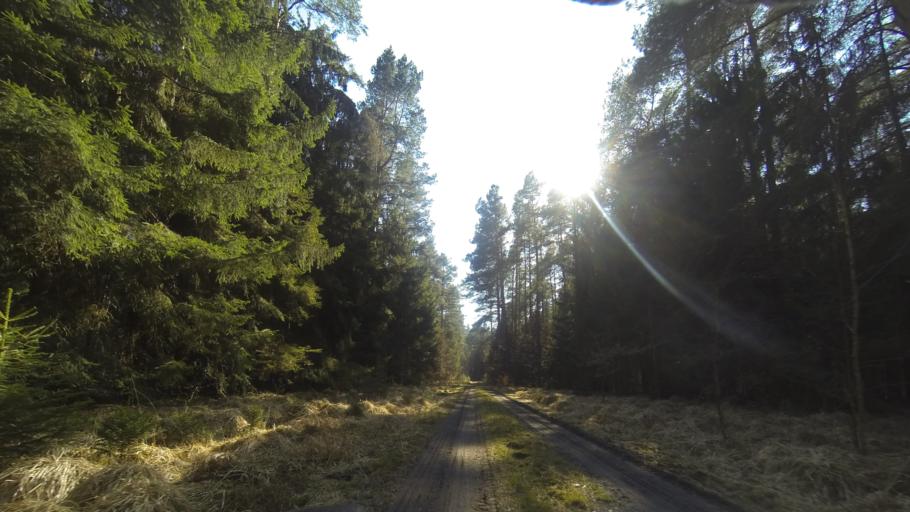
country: DE
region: Saxony
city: Laussnitz
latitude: 51.2552
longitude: 13.8448
